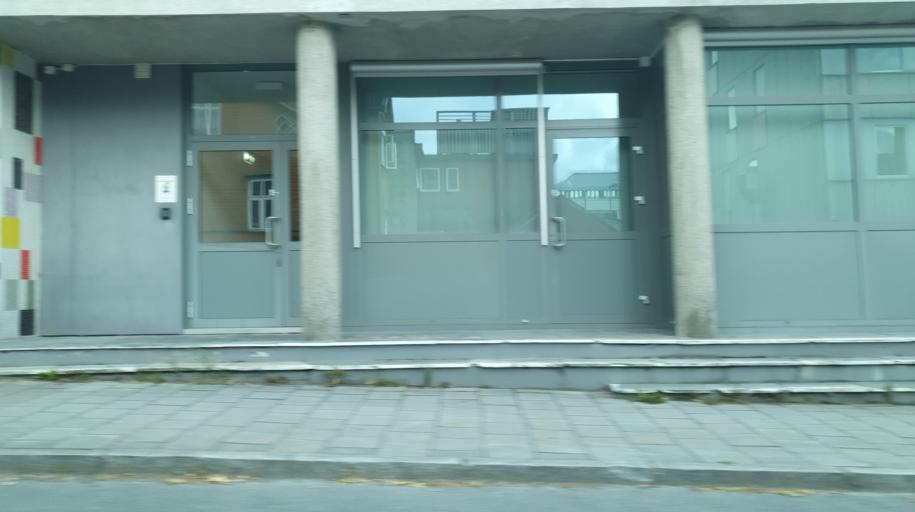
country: NO
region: Nord-Trondelag
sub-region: Levanger
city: Levanger
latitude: 63.7454
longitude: 11.2988
